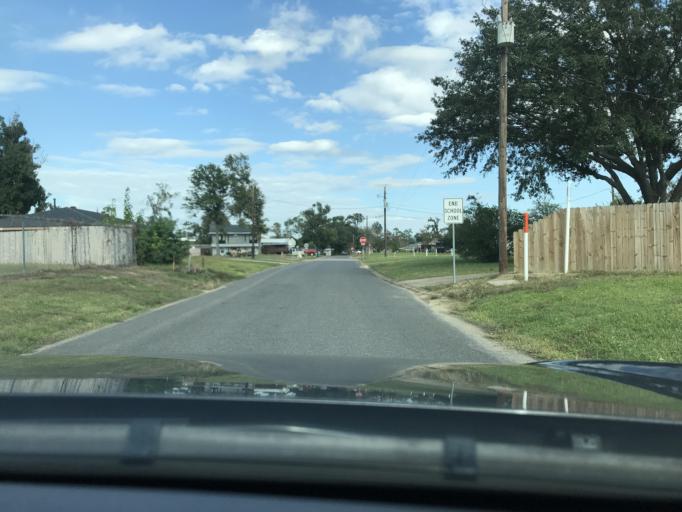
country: US
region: Louisiana
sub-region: Calcasieu Parish
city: Westlake
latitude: 30.2542
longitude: -93.2562
